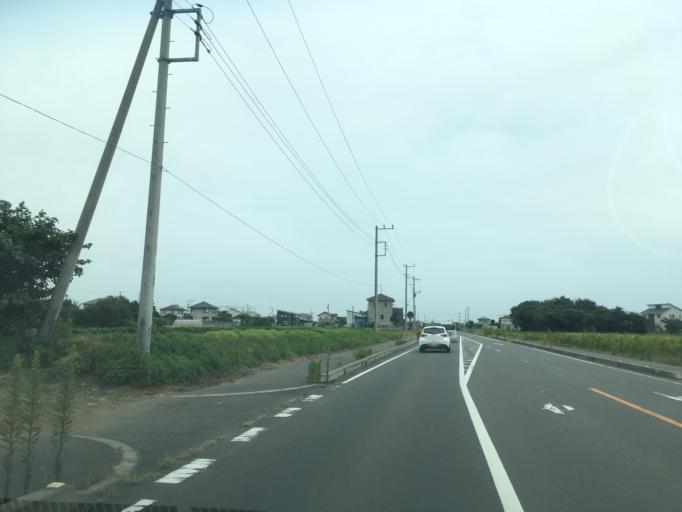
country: JP
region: Ibaraki
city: Hitachi-Naka
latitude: 36.4098
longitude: 140.5743
